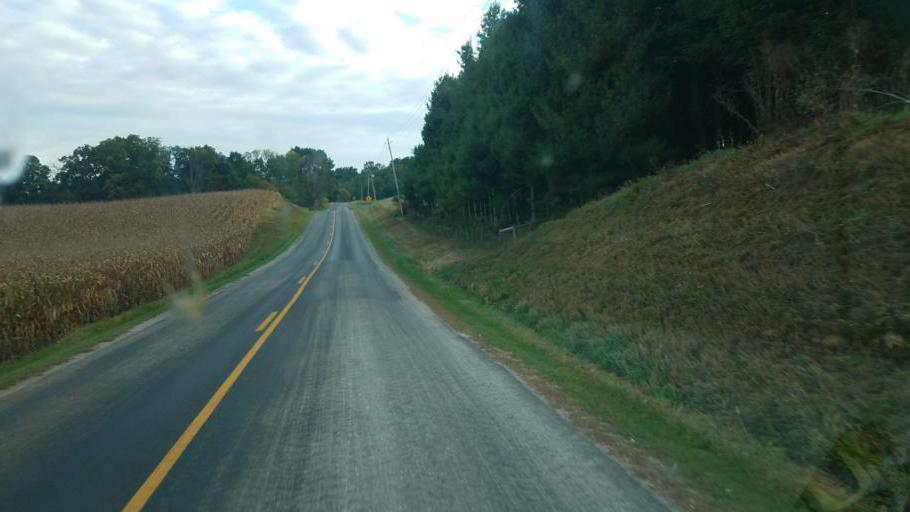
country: US
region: Ohio
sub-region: Ashland County
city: Loudonville
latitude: 40.7063
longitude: -82.1694
